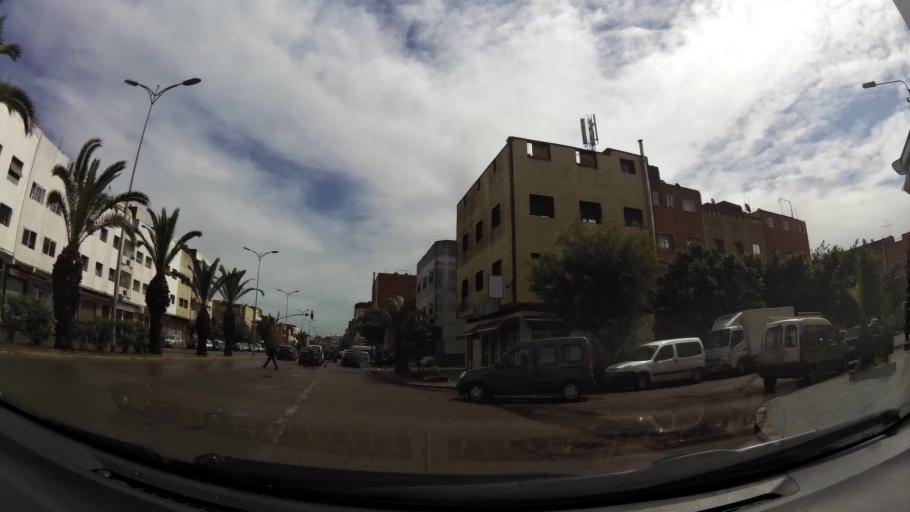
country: MA
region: Grand Casablanca
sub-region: Casablanca
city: Casablanca
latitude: 33.5525
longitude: -7.6784
